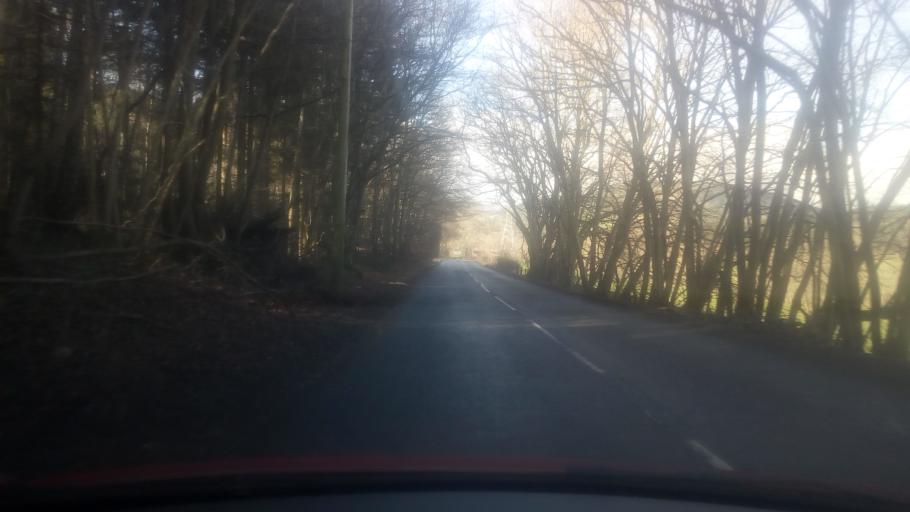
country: GB
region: Scotland
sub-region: The Scottish Borders
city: Selkirk
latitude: 55.5812
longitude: -2.8411
